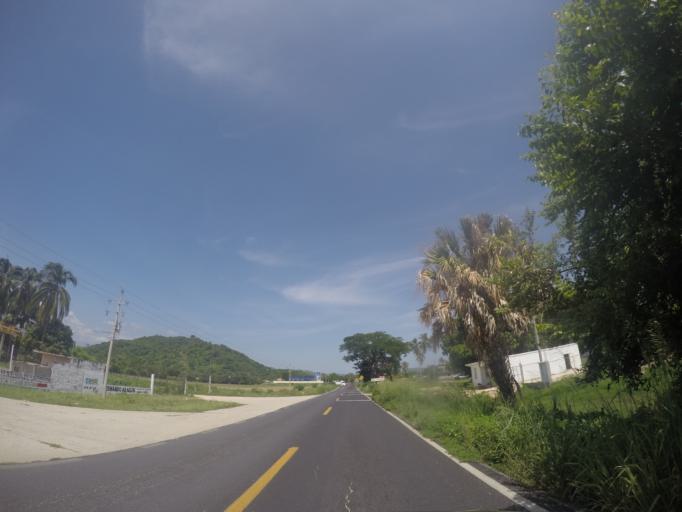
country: MX
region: Oaxaca
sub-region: Villa de Tututepec de Melchor Ocampo
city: Santa Rosa de Lima
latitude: 16.0111
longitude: -97.4543
